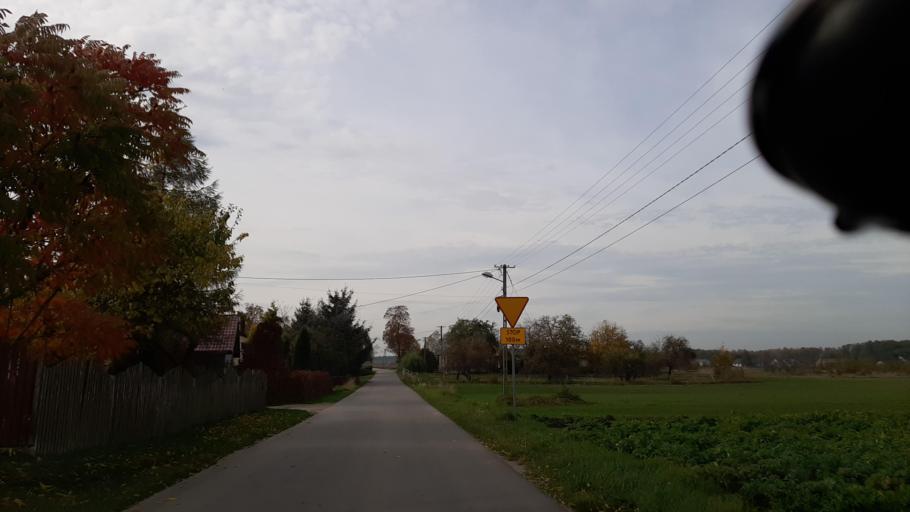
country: PL
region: Lublin Voivodeship
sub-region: Powiat lubelski
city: Garbow
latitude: 51.3921
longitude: 22.3174
